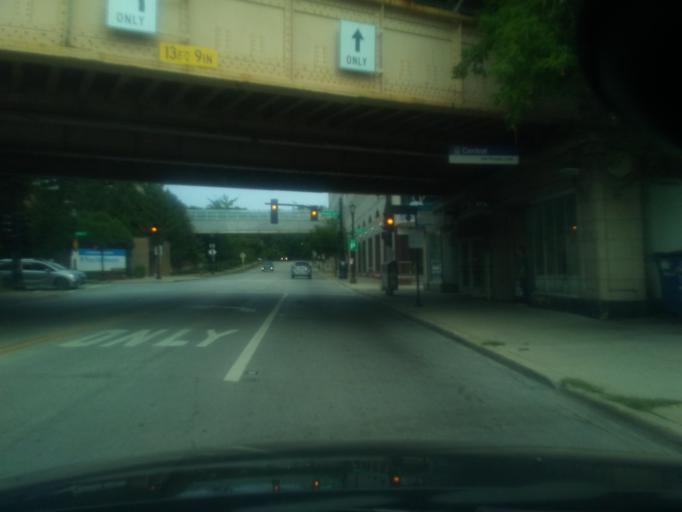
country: US
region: Illinois
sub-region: Cook County
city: Evanston
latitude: 42.0641
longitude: -87.6860
